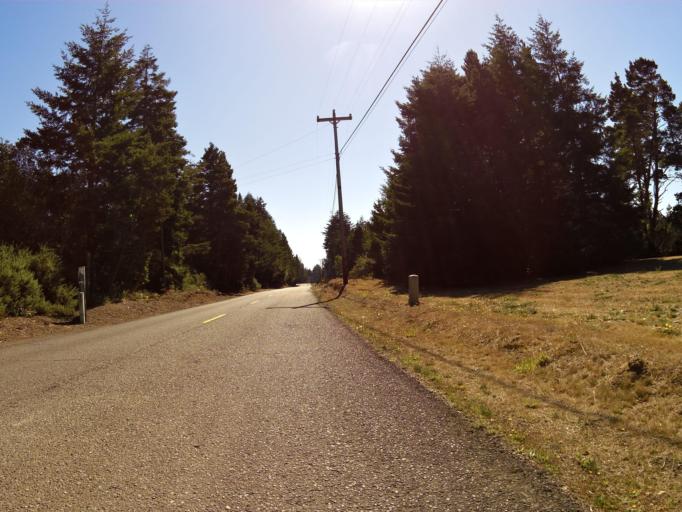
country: US
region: Oregon
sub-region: Coos County
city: Bandon
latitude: 43.1769
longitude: -124.3713
